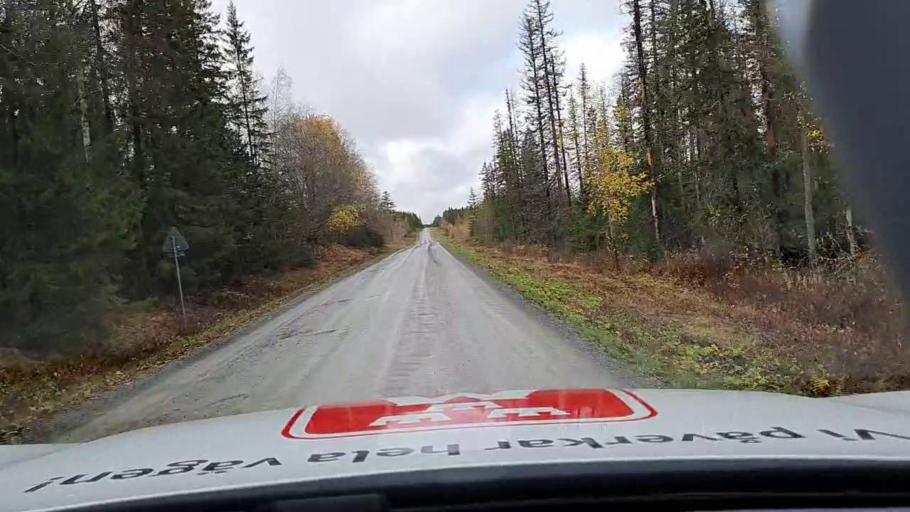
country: SE
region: Jaemtland
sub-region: Bergs Kommun
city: Hoverberg
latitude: 63.0045
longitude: 14.1317
